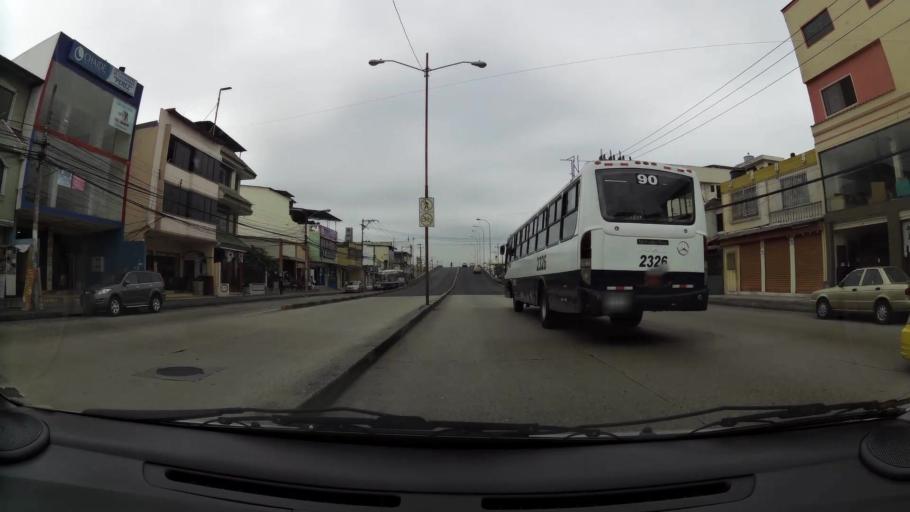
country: EC
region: Guayas
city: Eloy Alfaro
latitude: -2.1433
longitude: -79.8960
